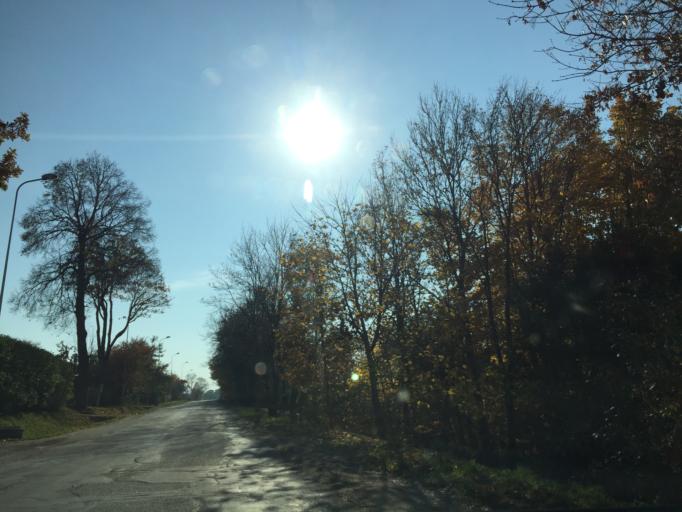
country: LV
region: Saldus Rajons
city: Saldus
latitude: 56.6752
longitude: 22.4954
